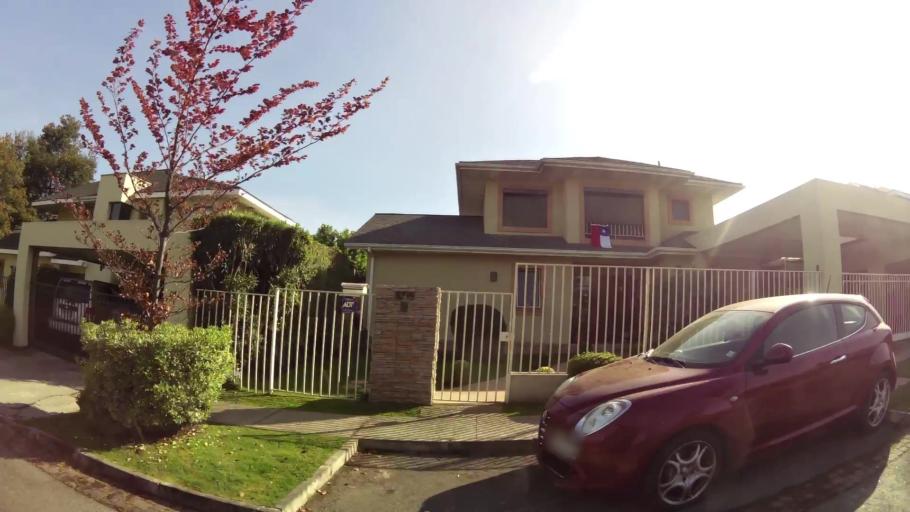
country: CL
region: Santiago Metropolitan
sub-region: Provincia de Santiago
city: Villa Presidente Frei, Nunoa, Santiago, Chile
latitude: -33.4921
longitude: -70.5519
